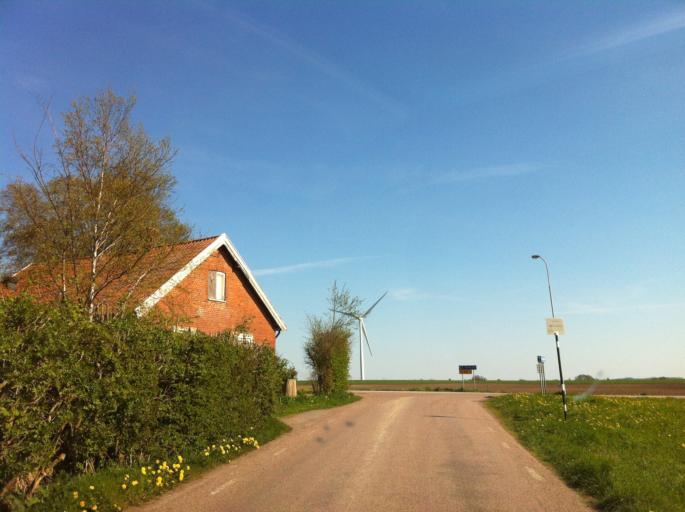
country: SE
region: Skane
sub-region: Svalovs Kommun
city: Kagerod
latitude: 55.9881
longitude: 13.0749
